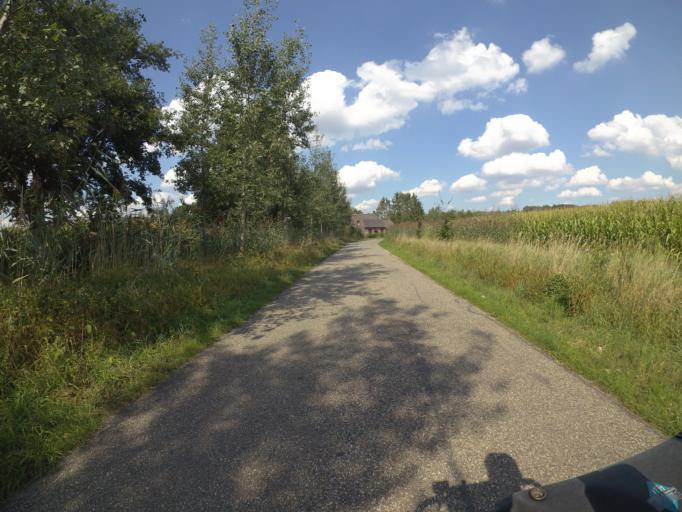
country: NL
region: North Brabant
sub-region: Gemeente Veghel
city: Eerde
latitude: 51.6173
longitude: 5.4786
